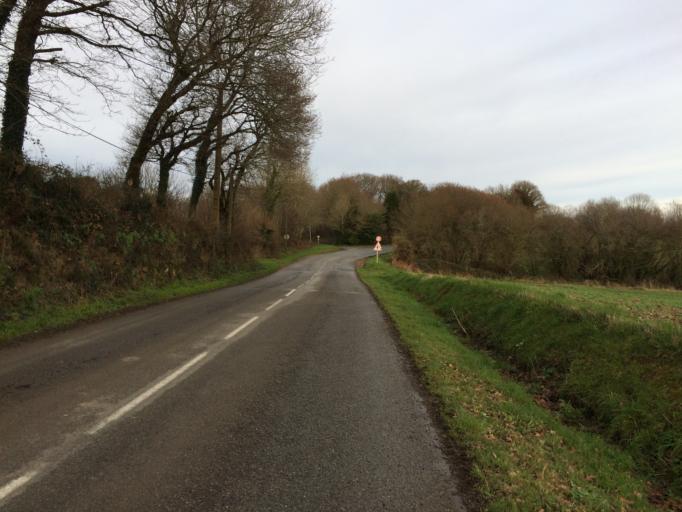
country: FR
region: Brittany
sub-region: Departement du Finistere
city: Daoulas
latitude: 48.3767
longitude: -4.2520
